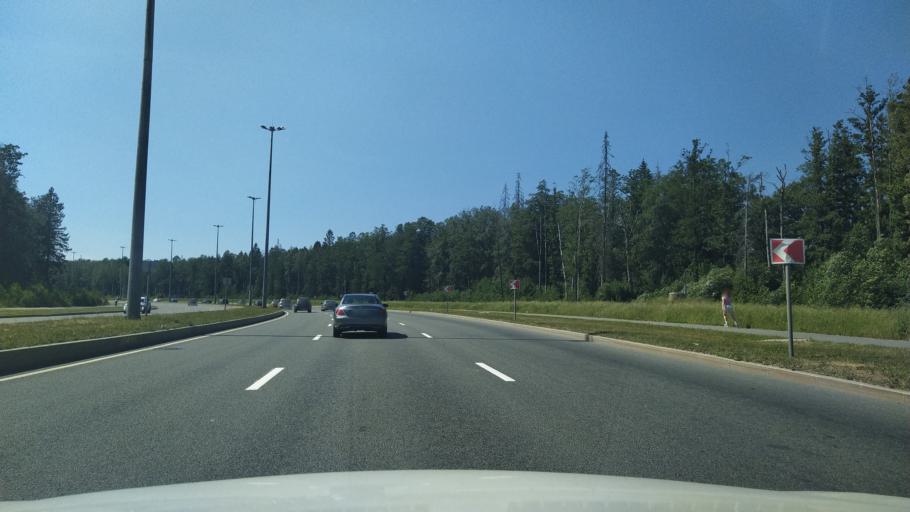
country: RU
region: St.-Petersburg
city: Levashovo
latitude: 60.0643
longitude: 30.2068
